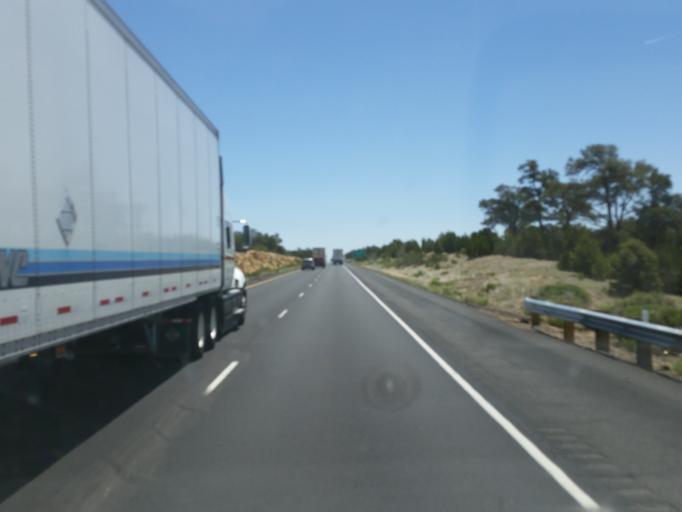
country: US
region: Arizona
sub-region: Coconino County
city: Flagstaff
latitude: 35.2036
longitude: -111.4890
